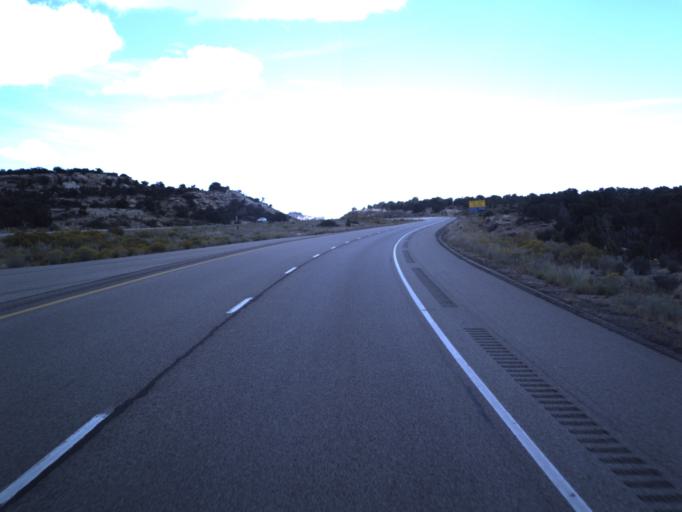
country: US
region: Utah
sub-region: Emery County
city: Ferron
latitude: 38.8630
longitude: -110.8443
